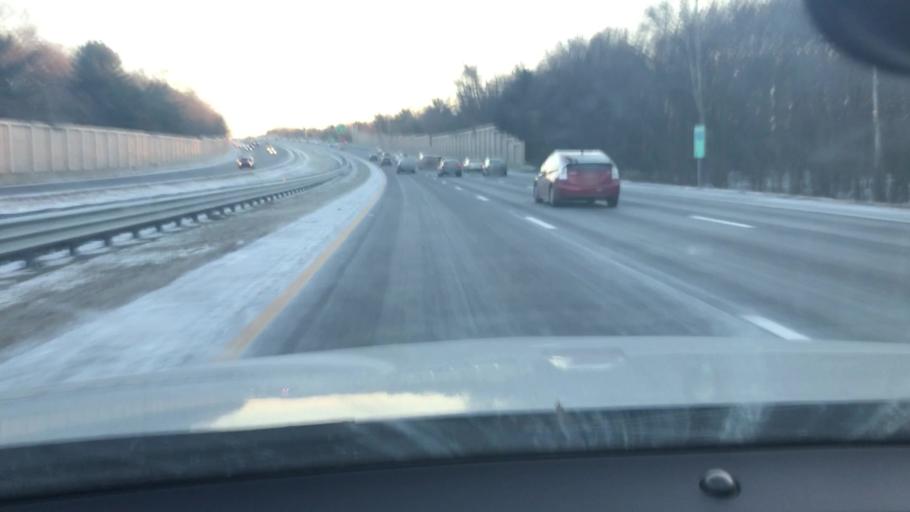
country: US
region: New Jersey
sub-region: Mercer County
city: Mercerville
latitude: 40.2397
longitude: -74.7019
